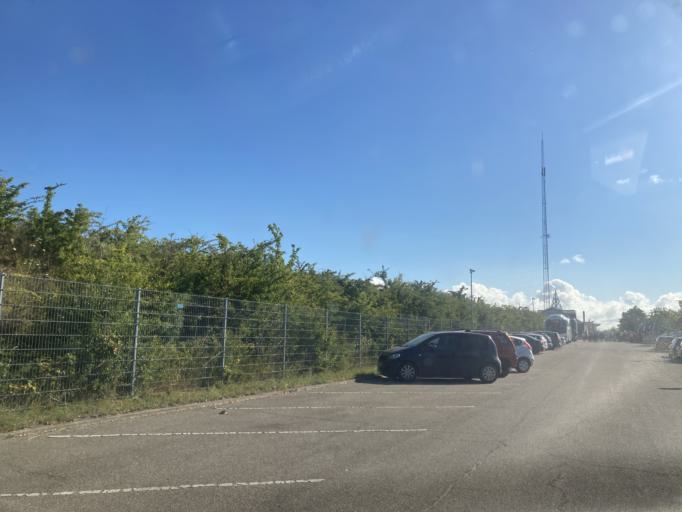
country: DK
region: Zealand
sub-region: Slagelse Kommune
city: Korsor
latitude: 55.3564
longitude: 11.1331
